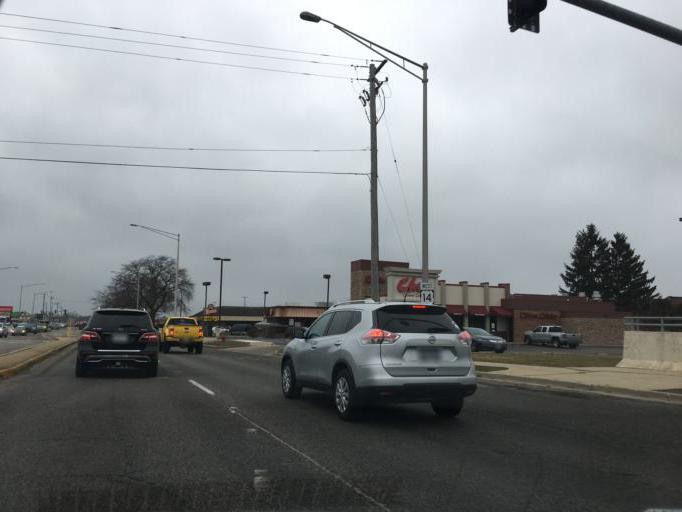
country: US
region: Illinois
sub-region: McHenry County
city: Crystal Lake
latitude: 42.2263
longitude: -88.3160
